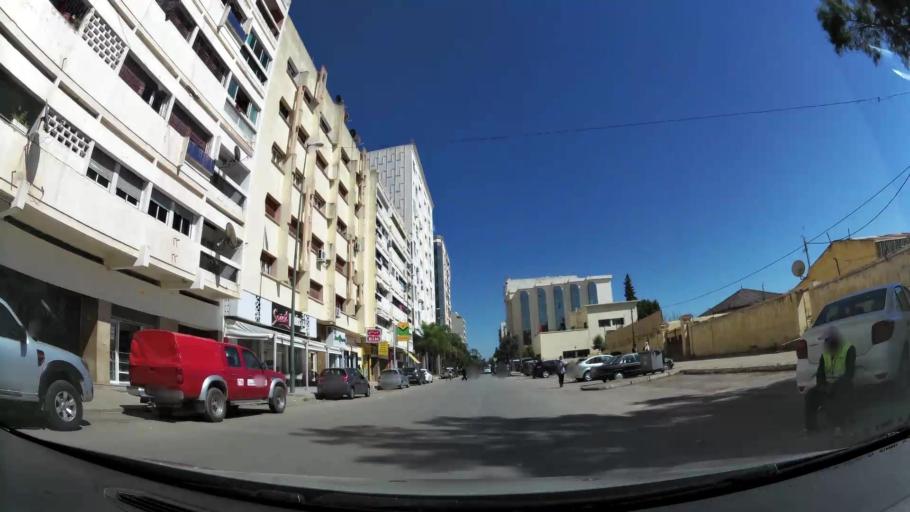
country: MA
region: Meknes-Tafilalet
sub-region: Meknes
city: Meknes
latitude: 33.8954
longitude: -5.5442
